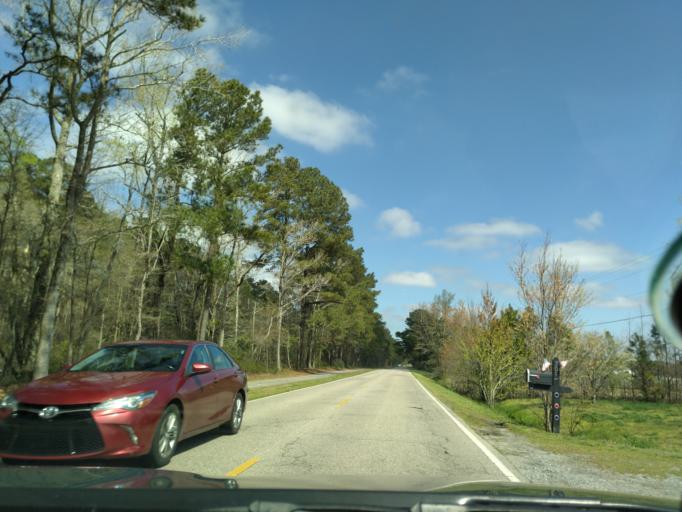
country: US
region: Virginia
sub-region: City of Portsmouth
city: Portsmouth Heights
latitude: 36.7051
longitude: -76.3549
